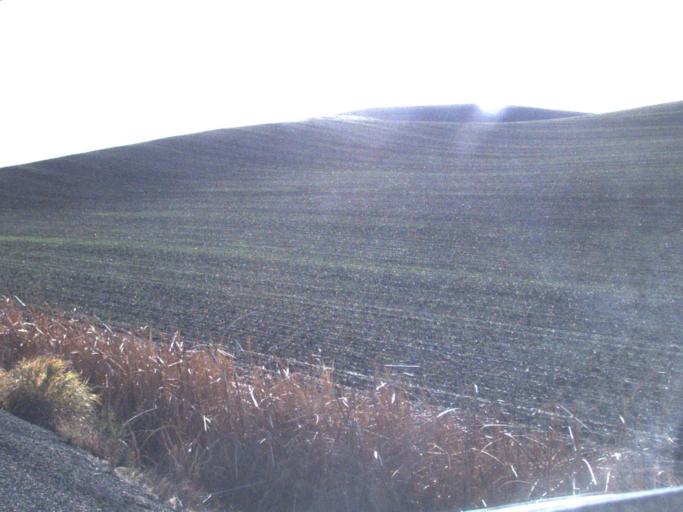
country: US
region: Washington
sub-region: Whitman County
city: Colfax
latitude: 46.7494
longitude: -117.3669
